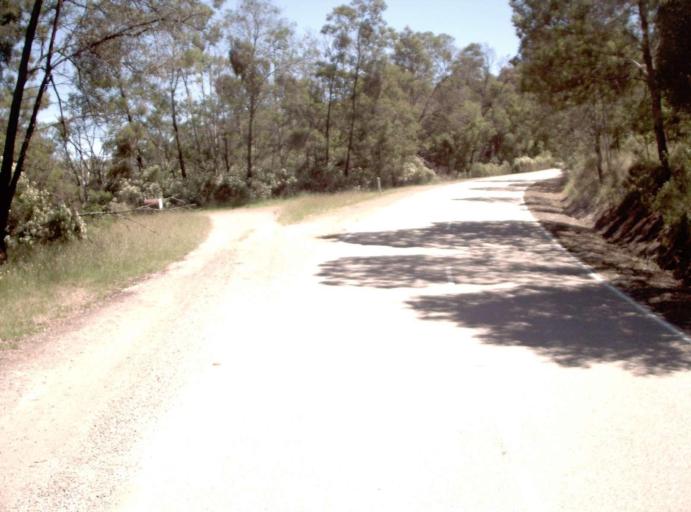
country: AU
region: Victoria
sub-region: East Gippsland
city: Lakes Entrance
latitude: -37.3195
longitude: 148.2447
